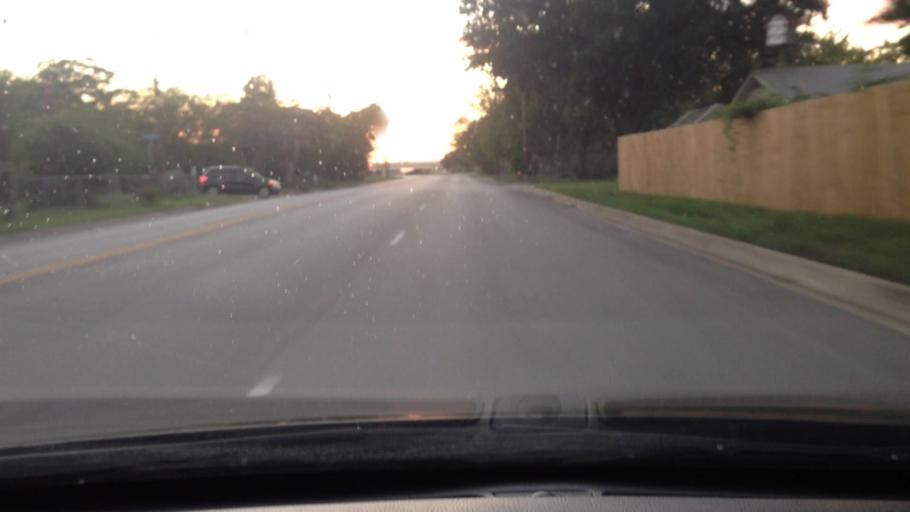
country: US
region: Texas
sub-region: Tarrant County
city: White Settlement
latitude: 32.7739
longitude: -97.4708
